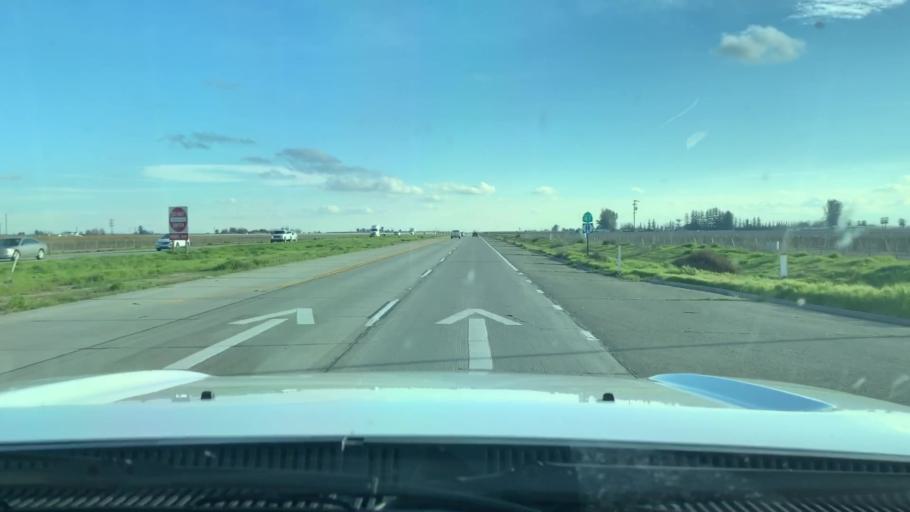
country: US
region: California
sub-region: Fresno County
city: Caruthers
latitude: 36.5617
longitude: -119.7863
